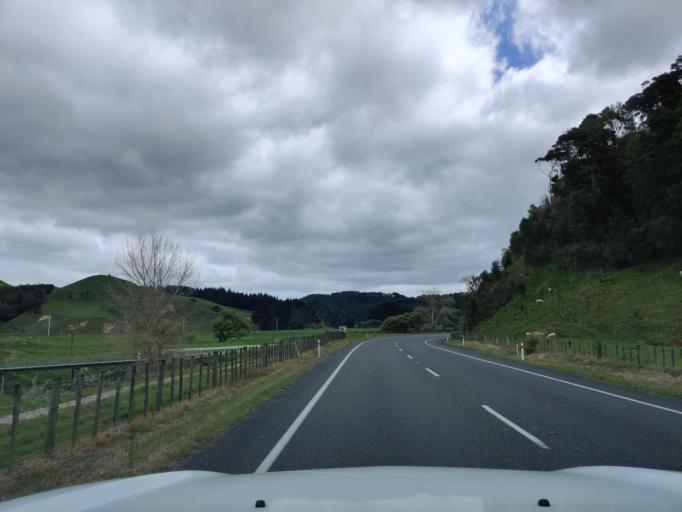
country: NZ
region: Manawatu-Wanganui
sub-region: Wanganui District
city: Wanganui
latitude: -39.8486
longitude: 175.1366
